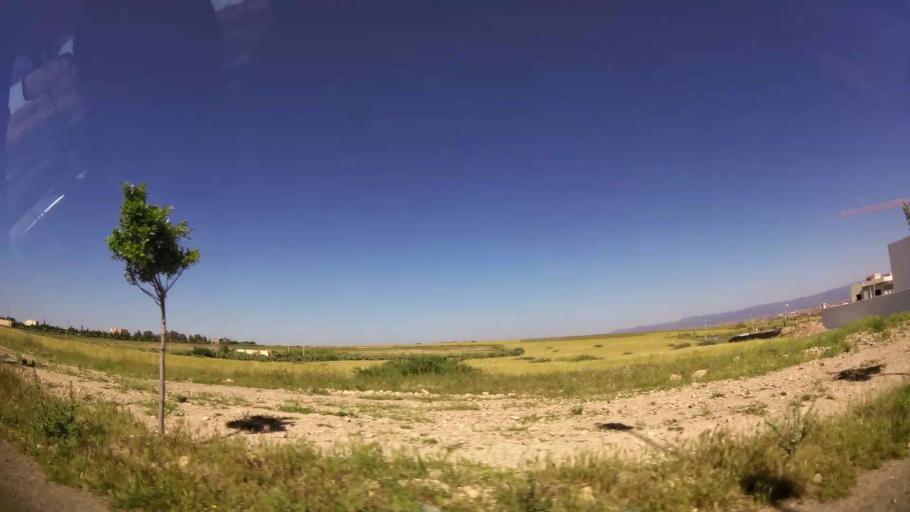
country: MA
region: Oriental
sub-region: Oujda-Angad
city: Oujda
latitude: 34.7350
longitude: -1.9188
